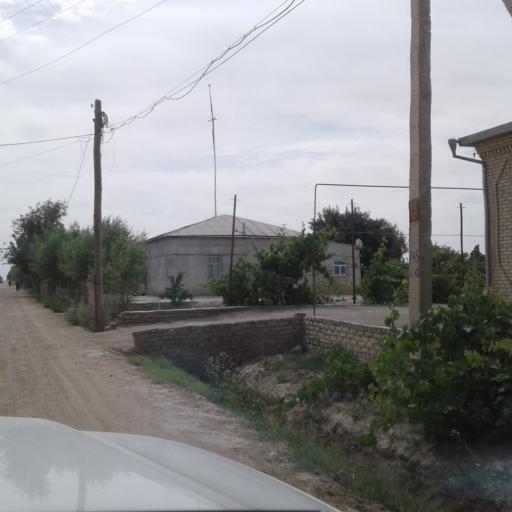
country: TM
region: Dasoguz
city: Tagta
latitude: 41.6016
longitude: 59.8476
